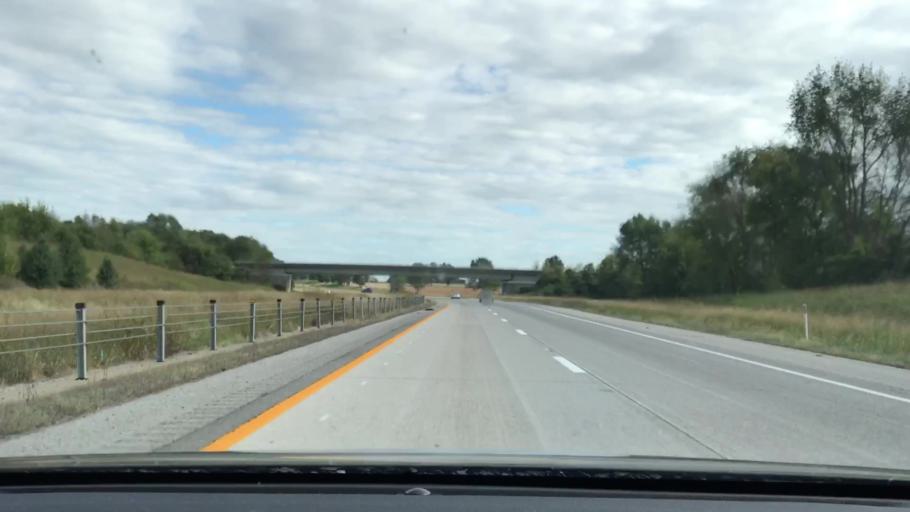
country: US
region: Kentucky
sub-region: Christian County
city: Hopkinsville
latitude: 36.8307
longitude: -87.6623
